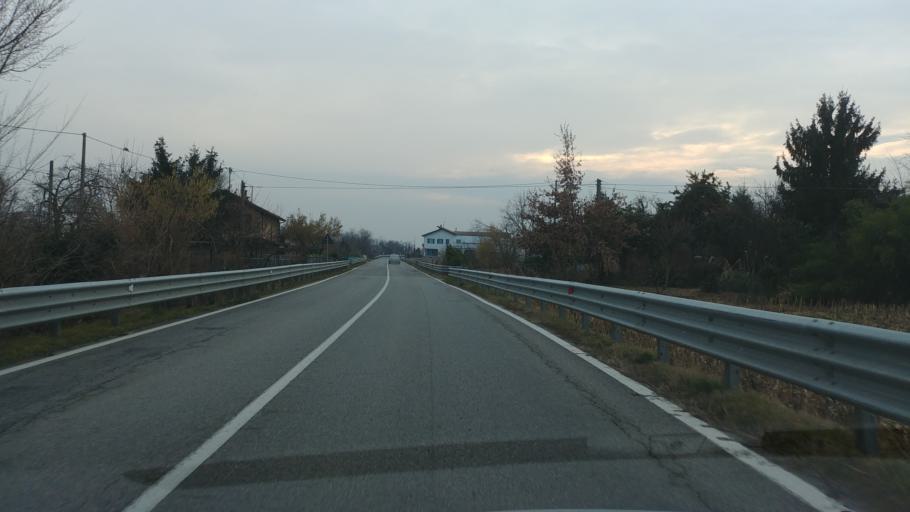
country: IT
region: Piedmont
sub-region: Provincia di Cuneo
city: Castelletto Stura
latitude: 44.4521
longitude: 7.6214
